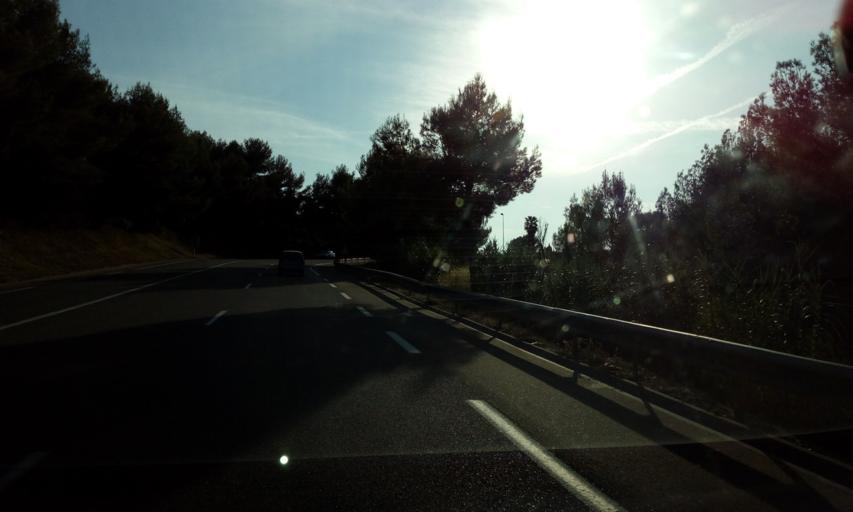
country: FR
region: Provence-Alpes-Cote d'Azur
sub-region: Departement du Var
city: Bandol
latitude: 43.1498
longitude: 5.7526
